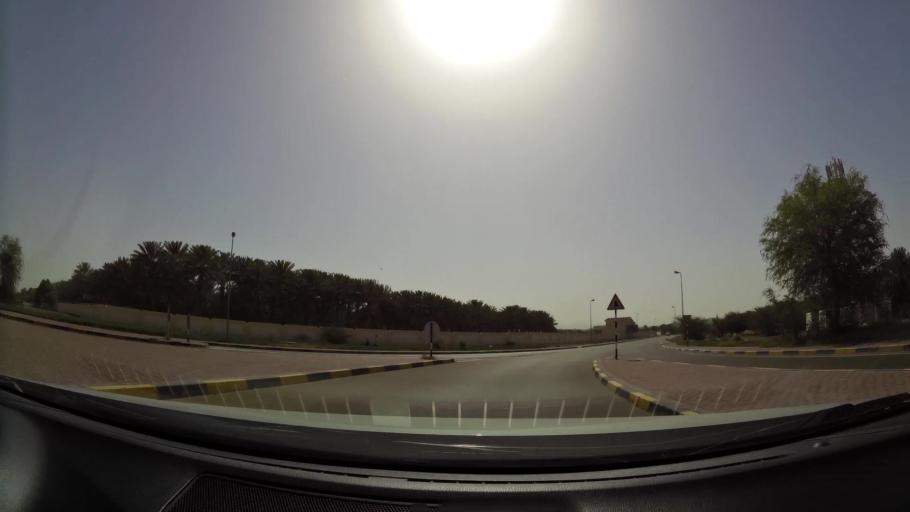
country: OM
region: Al Buraimi
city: Al Buraymi
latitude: 24.3151
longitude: 55.7975
